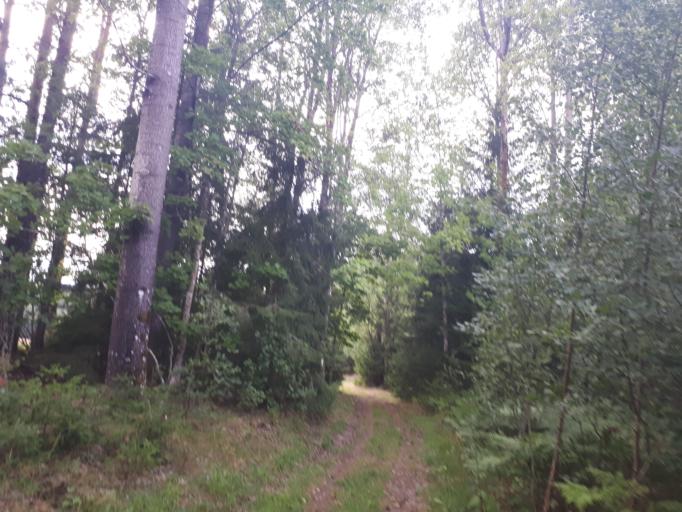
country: SE
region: Soedermanland
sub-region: Flens Kommun
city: Halleforsnas
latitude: 59.0706
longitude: 16.3891
